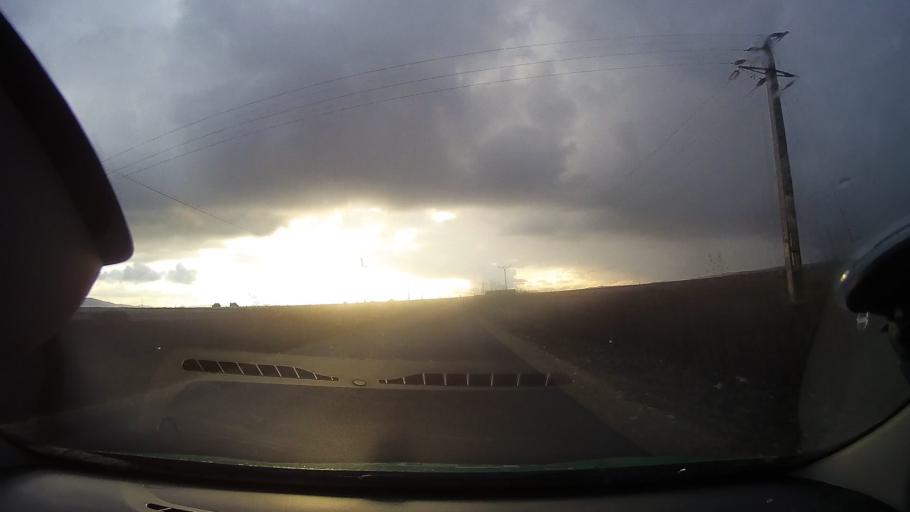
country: RO
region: Cluj
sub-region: Comuna Luna
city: Luncani
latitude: 46.4534
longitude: 23.9586
